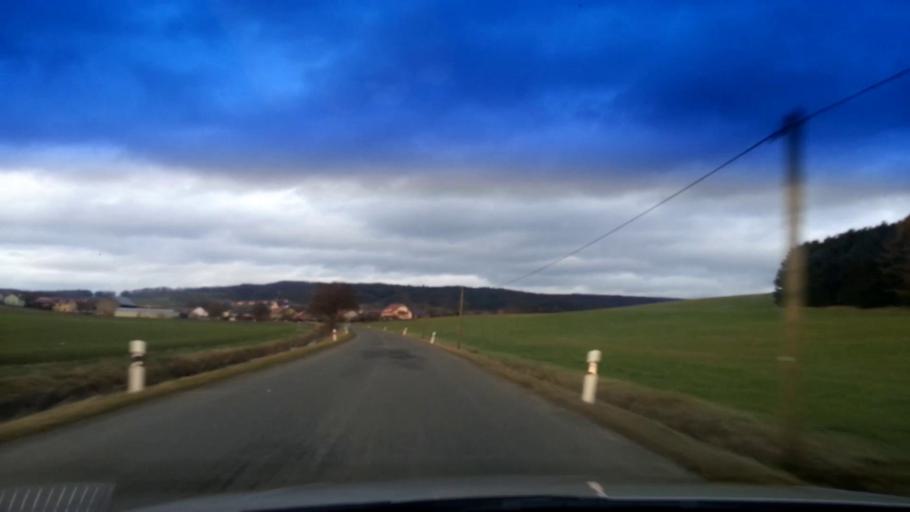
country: DE
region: Bavaria
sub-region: Upper Franconia
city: Schesslitz
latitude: 49.9989
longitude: 11.0143
